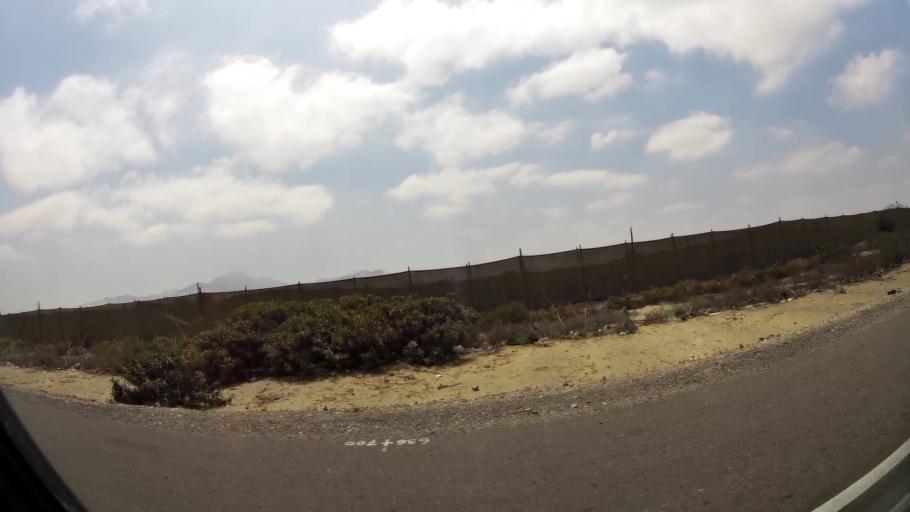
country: PE
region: La Libertad
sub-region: Ascope
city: Paijan
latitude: -7.6607
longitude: -79.3349
